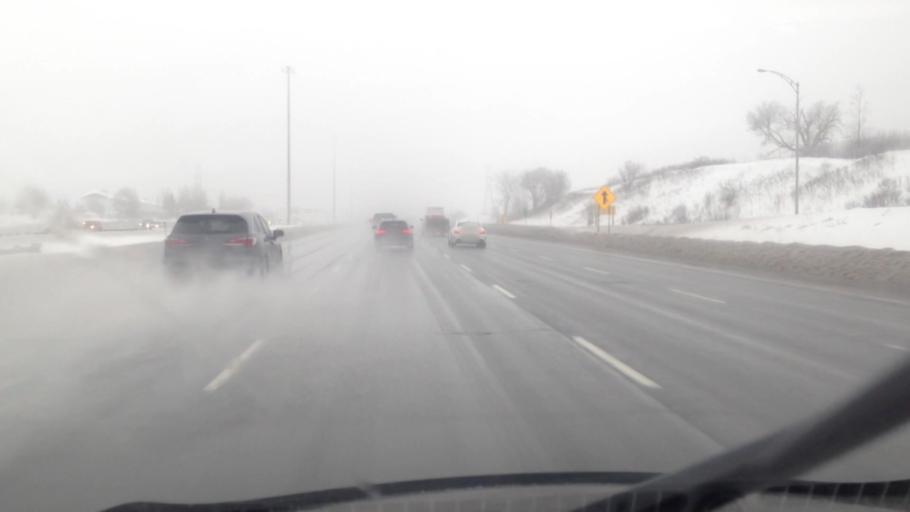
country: CA
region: Quebec
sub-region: Laurentides
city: Blainville
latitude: 45.6453
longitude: -73.8663
